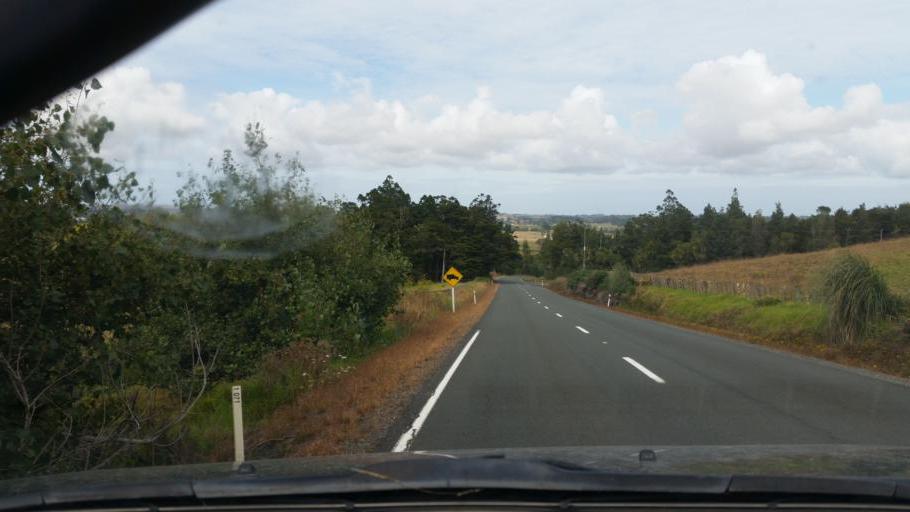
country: NZ
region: Northland
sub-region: Kaipara District
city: Dargaville
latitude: -35.9488
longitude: 173.9037
